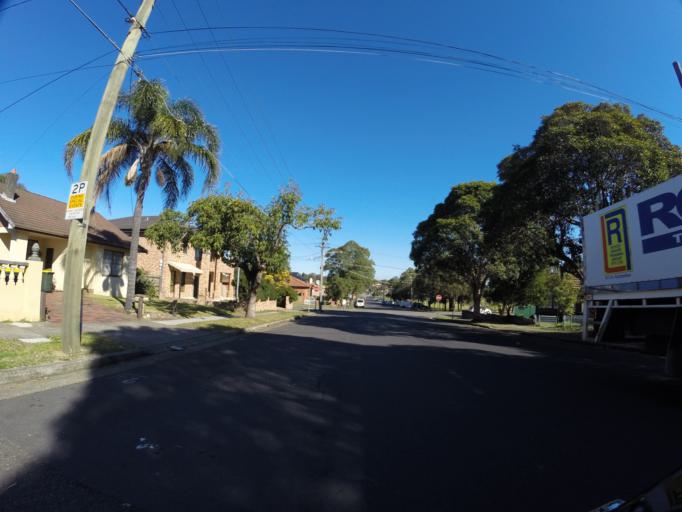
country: AU
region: New South Wales
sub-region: Auburn
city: Lidcombe
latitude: -33.8579
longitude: 151.0553
